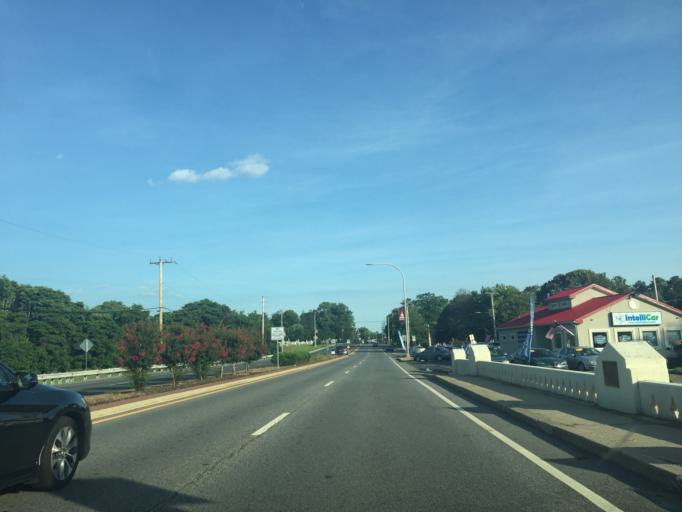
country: US
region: Delaware
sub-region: Kent County
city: Smyrna
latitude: 39.2973
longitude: -75.6001
